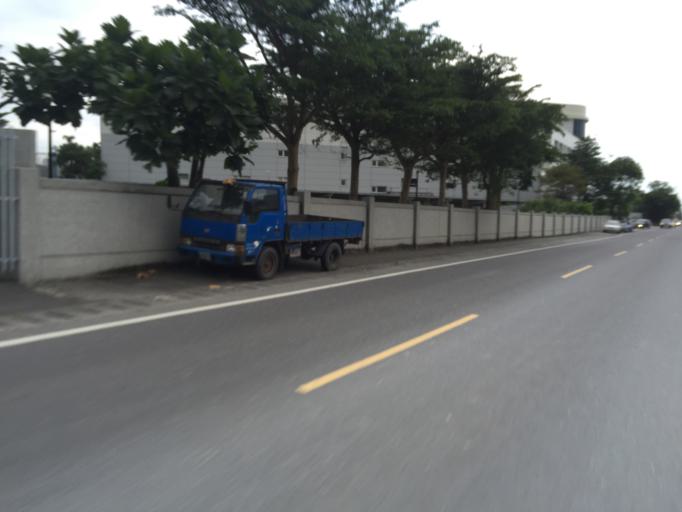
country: TW
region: Taiwan
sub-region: Yilan
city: Yilan
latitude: 24.7808
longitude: 121.7333
